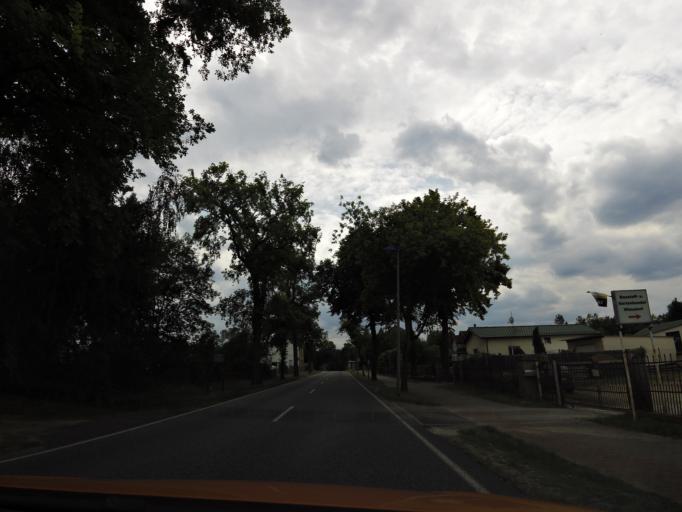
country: DE
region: Brandenburg
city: Zossen
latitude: 52.1479
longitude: 13.4802
